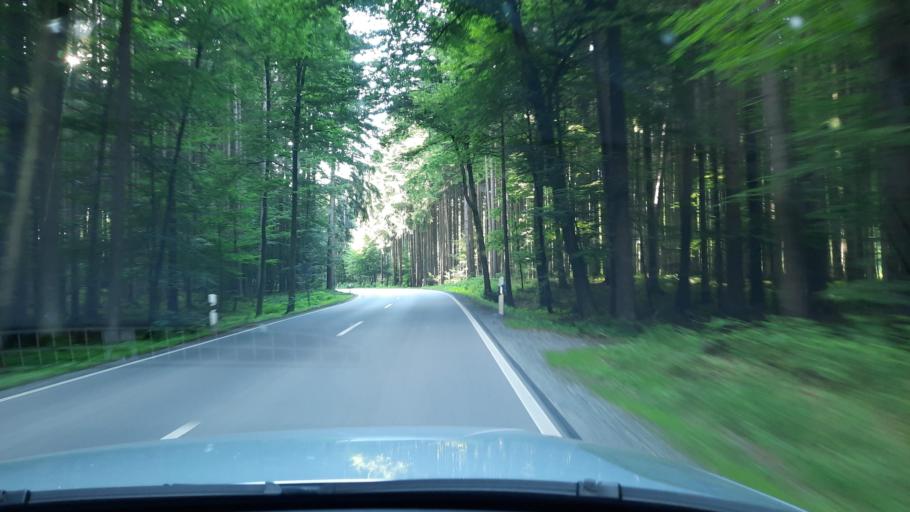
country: DE
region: Bavaria
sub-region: Upper Bavaria
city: Oberpframmern
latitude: 48.0118
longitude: 11.8378
